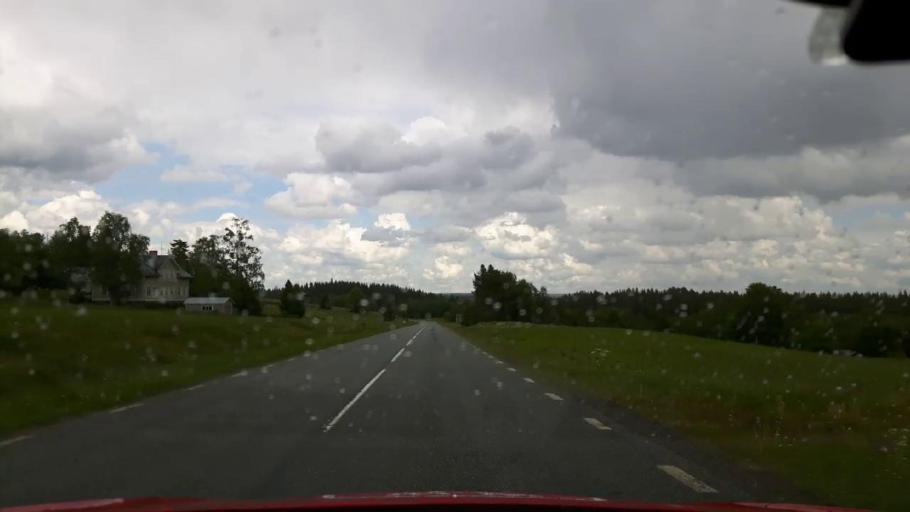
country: SE
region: Jaemtland
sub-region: Krokoms Kommun
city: Krokom
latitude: 63.4914
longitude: 14.2085
